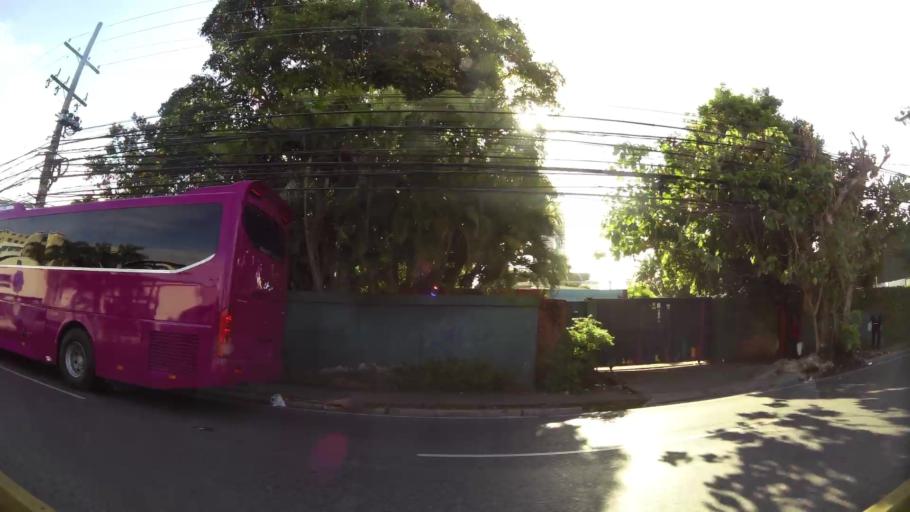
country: DO
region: Nacional
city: La Julia
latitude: 18.4767
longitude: -69.9313
